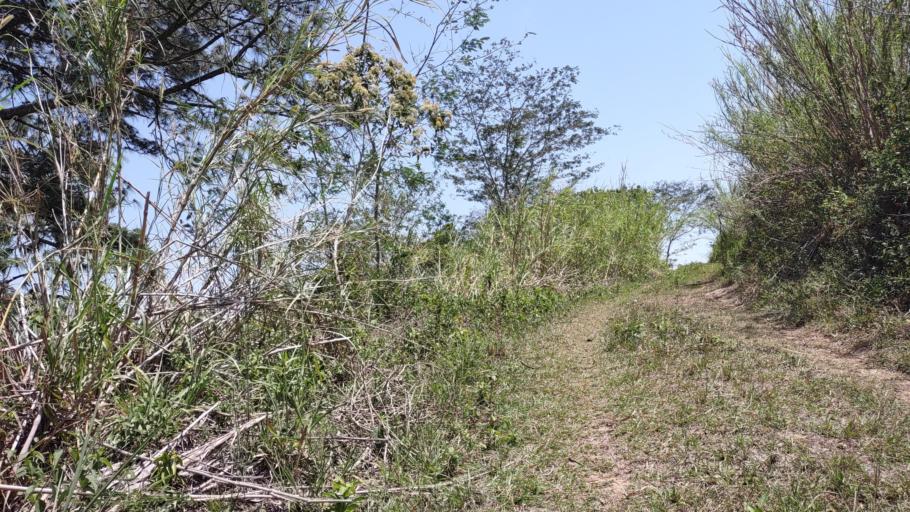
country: MX
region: Veracruz
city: El Castillo
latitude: 19.5526
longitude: -96.8418
